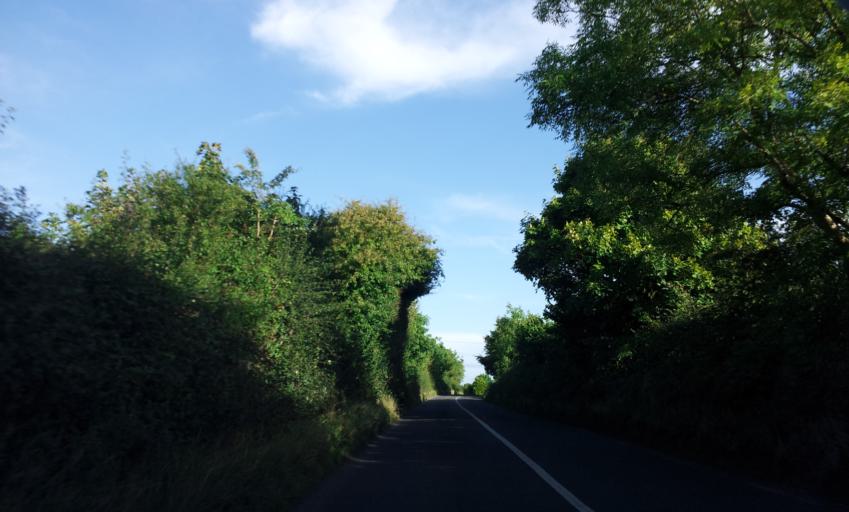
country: IE
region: Munster
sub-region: An Clar
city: Ennis
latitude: 52.9293
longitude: -9.0580
